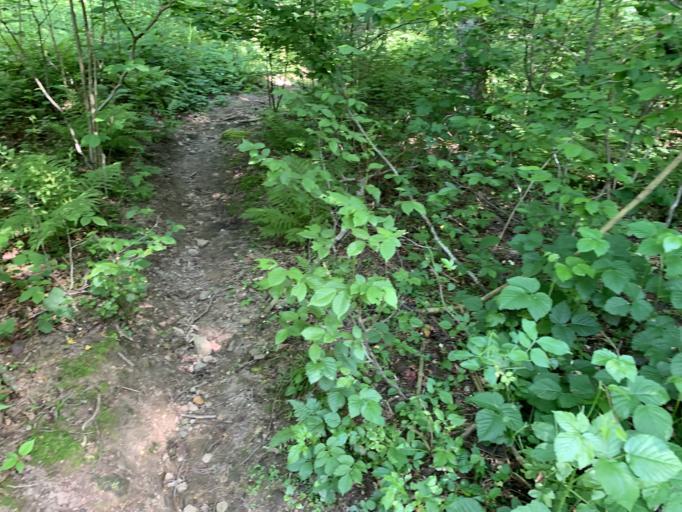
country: RU
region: Krasnodarskiy
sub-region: Sochi City
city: Lazarevskoye
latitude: 43.9512
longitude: 39.3227
